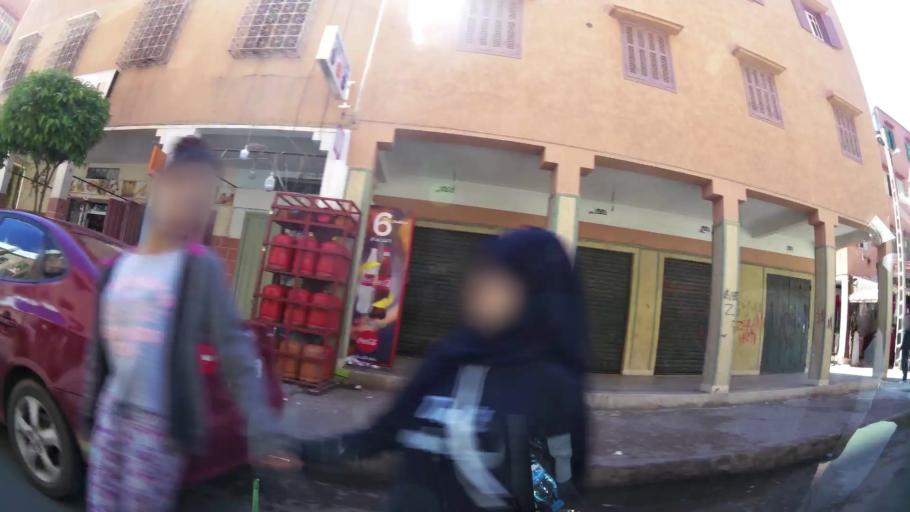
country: MA
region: Marrakech-Tensift-Al Haouz
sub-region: Marrakech
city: Marrakesh
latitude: 31.6313
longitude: -8.0605
